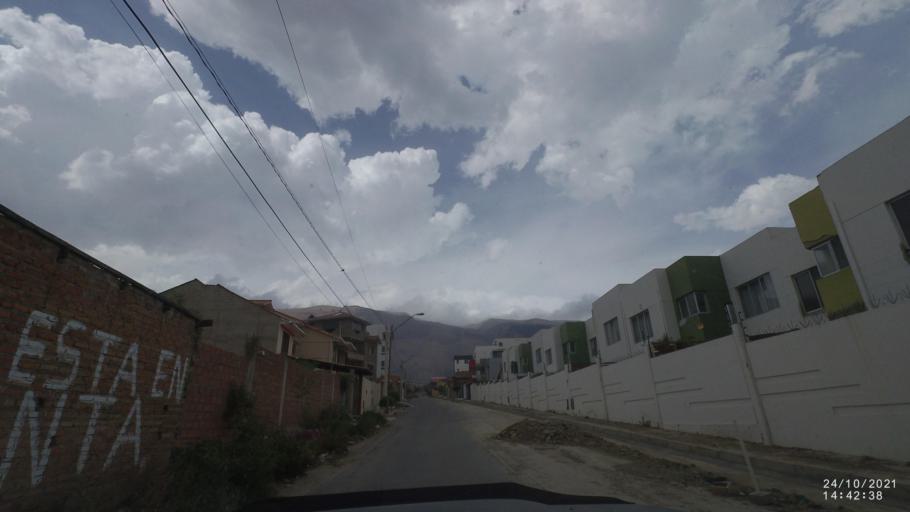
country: BO
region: Cochabamba
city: Cochabamba
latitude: -17.3514
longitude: -66.1779
